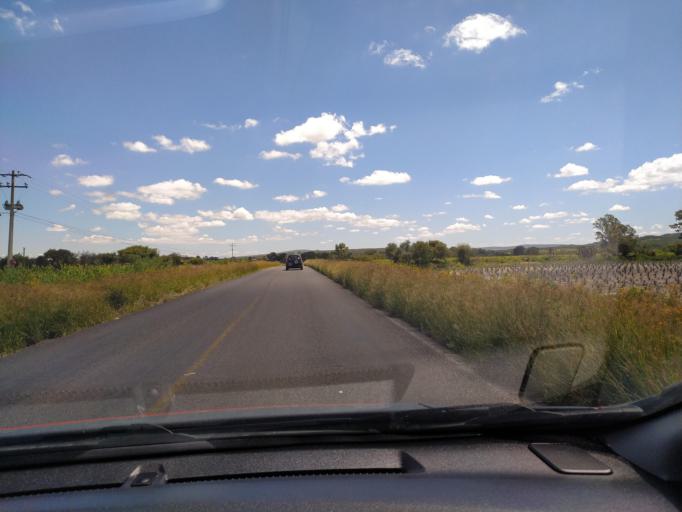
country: MX
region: Jalisco
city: San Diego de Alejandria
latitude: 21.0058
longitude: -102.0569
